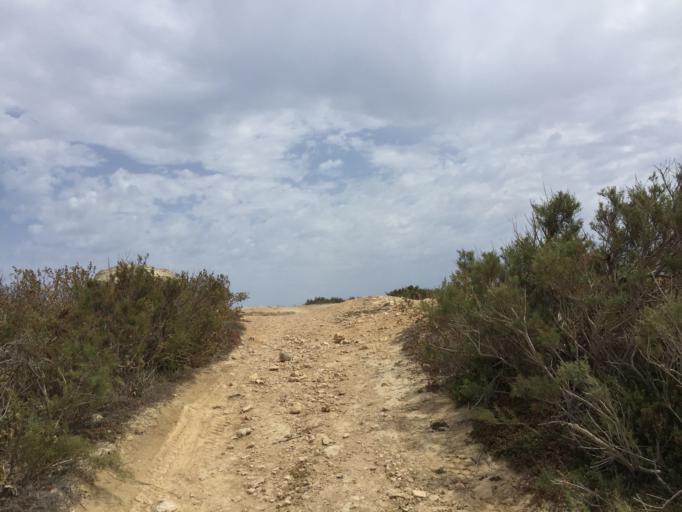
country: MT
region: Iz-Zebbug
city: Zebbug
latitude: 36.0787
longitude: 14.2494
